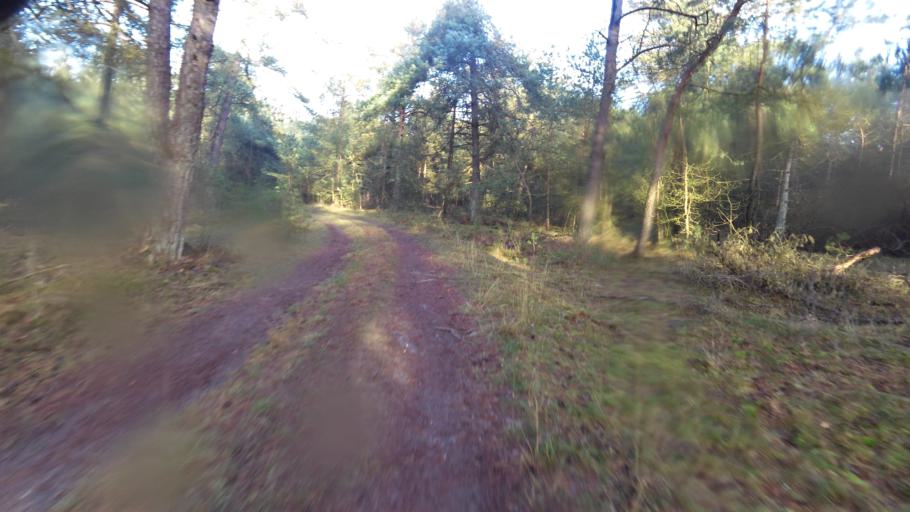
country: NL
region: Gelderland
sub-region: Gemeente Barneveld
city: Garderen
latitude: 52.2027
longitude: 5.7392
